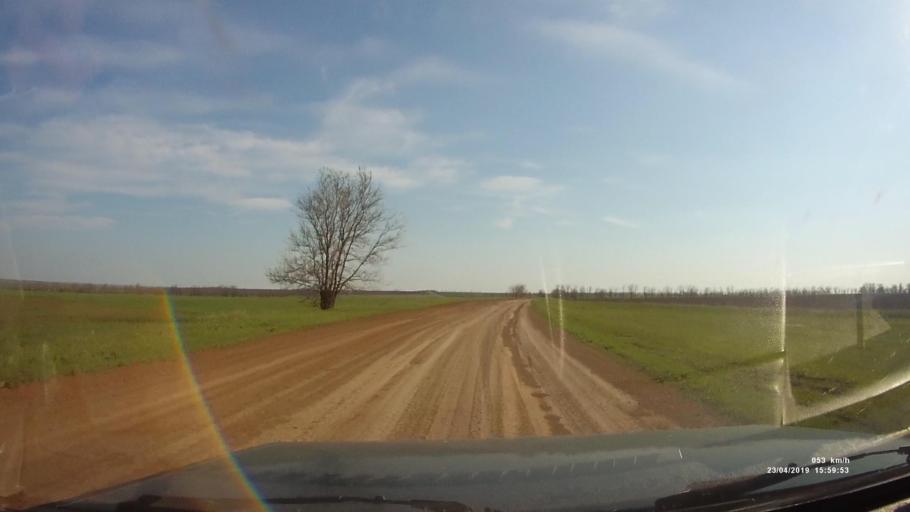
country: RU
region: Rostov
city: Remontnoye
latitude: 46.5134
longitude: 43.1093
